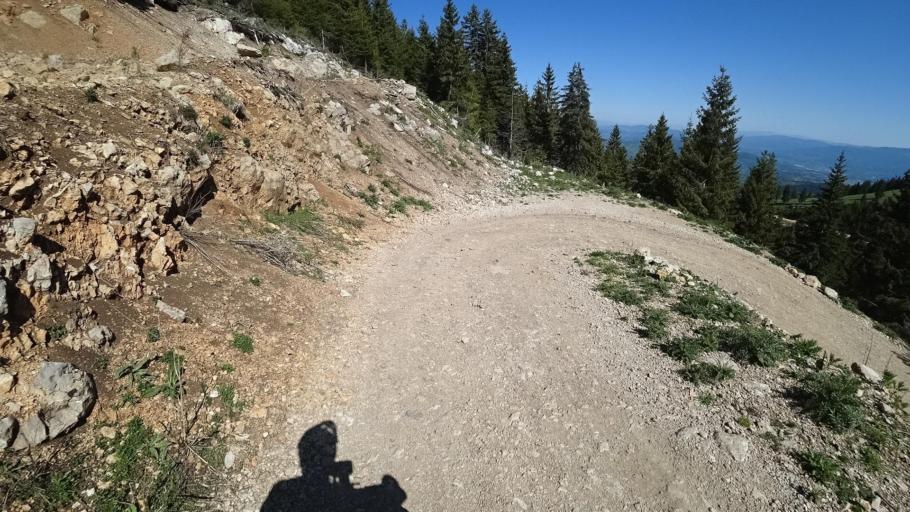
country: BA
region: Federation of Bosnia and Herzegovina
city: Travnik
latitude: 44.2922
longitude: 17.6878
